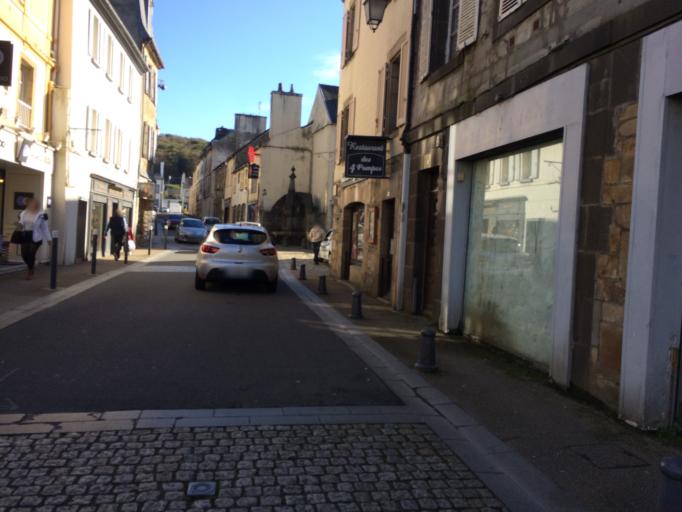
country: FR
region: Brittany
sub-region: Departement du Finistere
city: Landerneau
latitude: 48.4499
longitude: -4.2489
